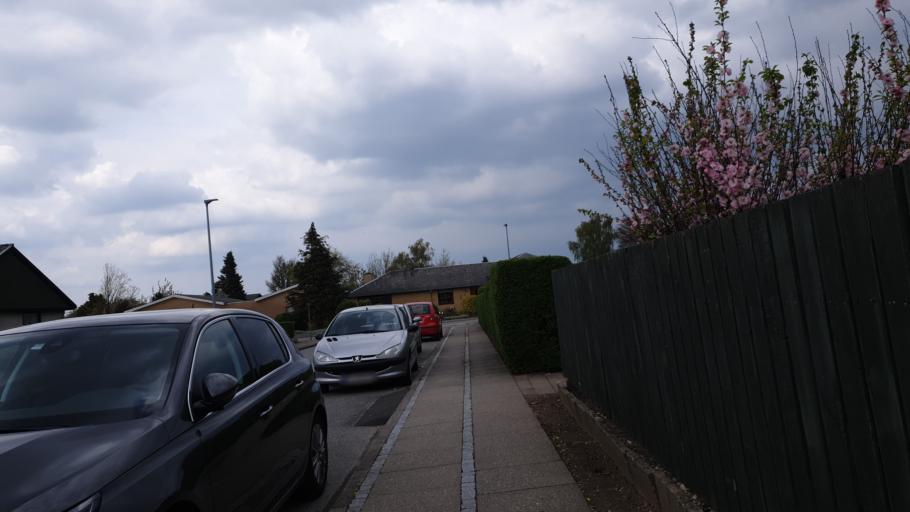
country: DK
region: Central Jutland
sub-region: Hedensted Kommune
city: Hedensted
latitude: 55.8000
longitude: 9.6930
